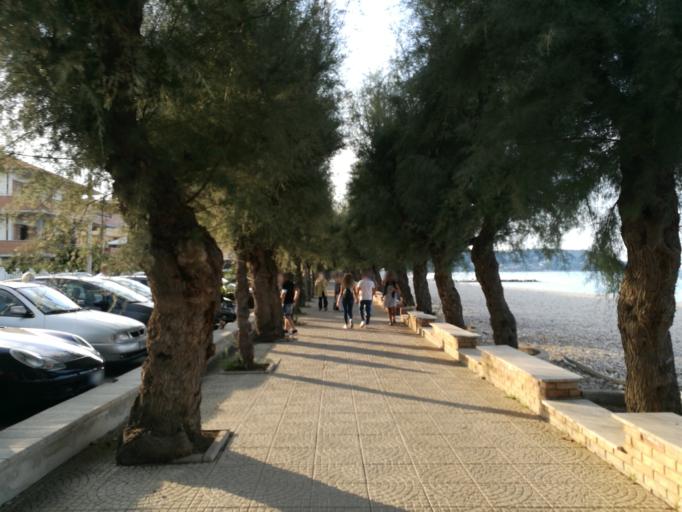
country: IT
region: Abruzzo
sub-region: Provincia di Chieti
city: Fossacesia
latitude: 42.2474
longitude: 14.5159
